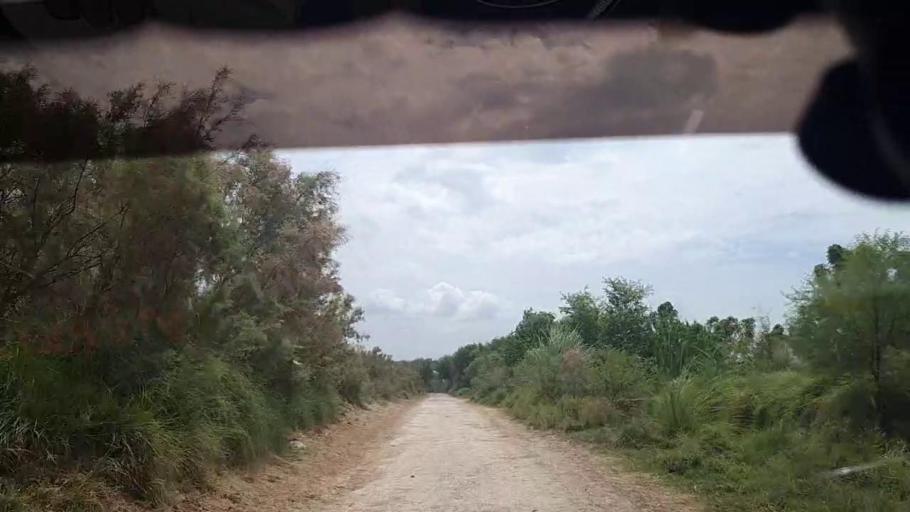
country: PK
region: Sindh
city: Rustam jo Goth
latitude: 28.0418
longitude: 68.9409
